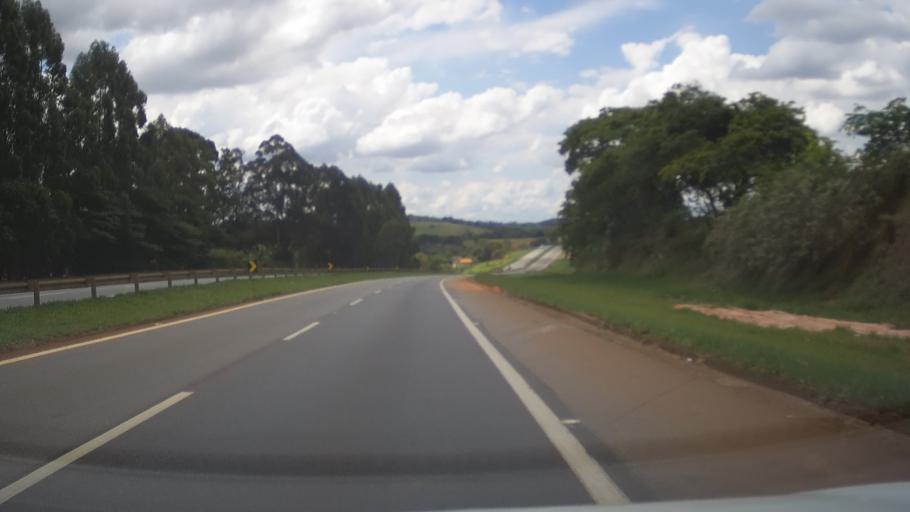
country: BR
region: Minas Gerais
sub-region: Nepomuceno
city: Nepomuceno
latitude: -21.2390
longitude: -45.1353
